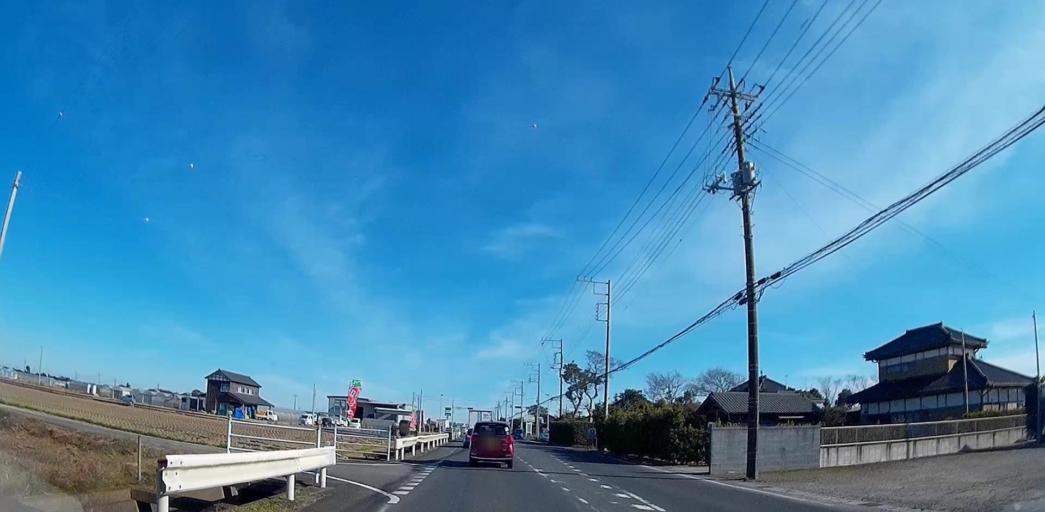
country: JP
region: Chiba
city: Asahi
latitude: 35.7435
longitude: 140.6146
